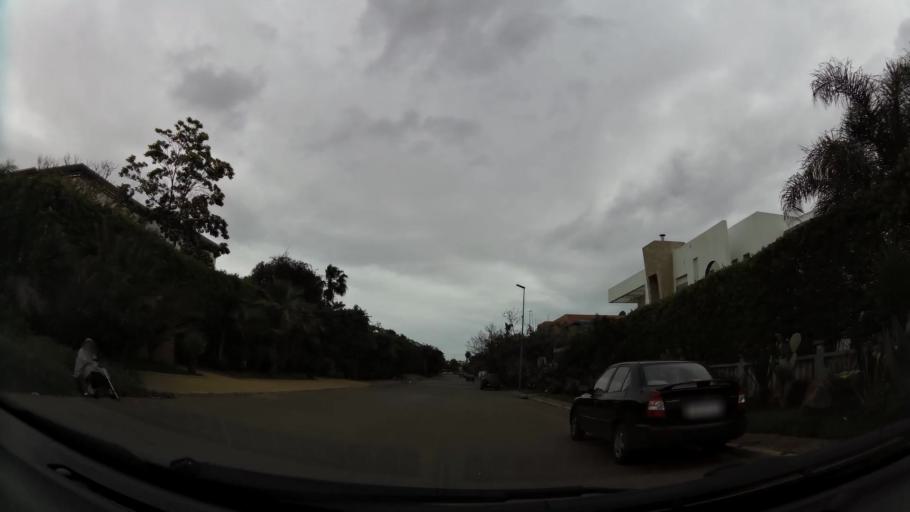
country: MA
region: Grand Casablanca
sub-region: Casablanca
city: Casablanca
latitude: 33.5415
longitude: -7.6368
